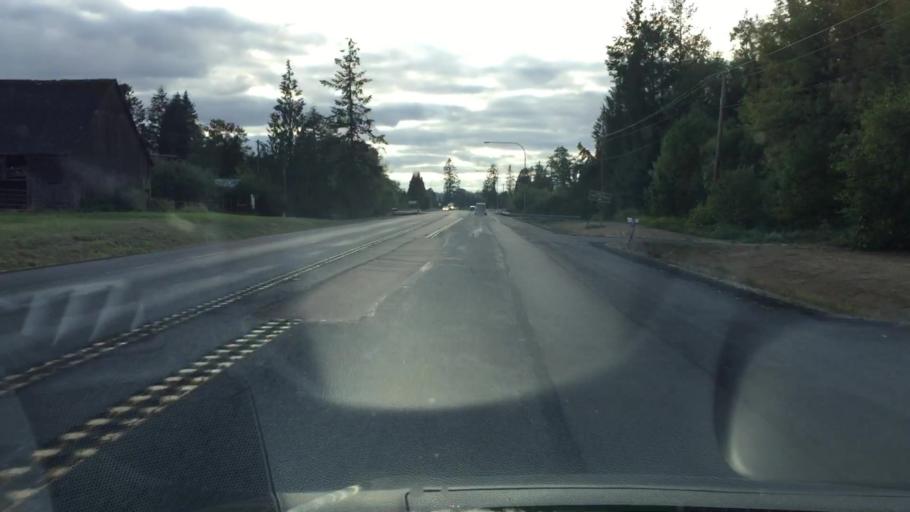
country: US
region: Washington
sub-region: Lewis County
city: Napavine
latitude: 46.5322
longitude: -122.7376
